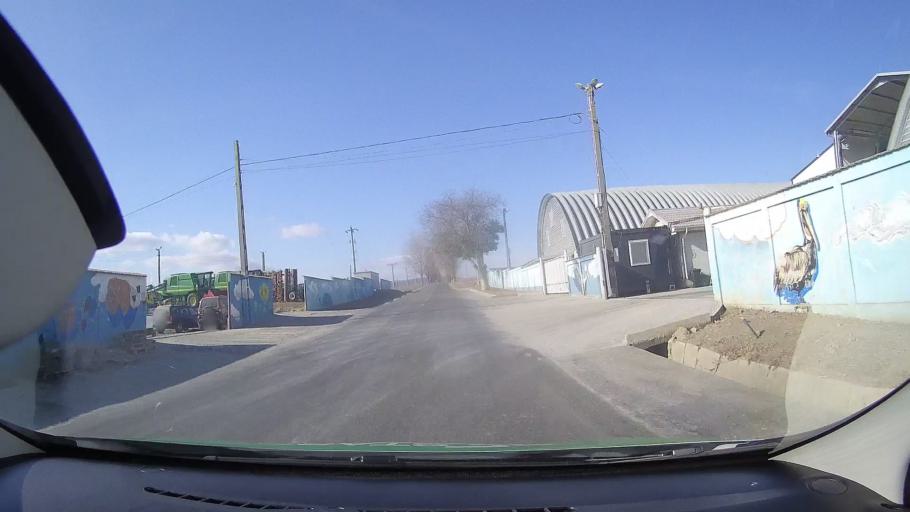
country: RO
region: Tulcea
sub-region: Comuna Sarichioi
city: Enisala
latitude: 44.8786
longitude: 28.8036
